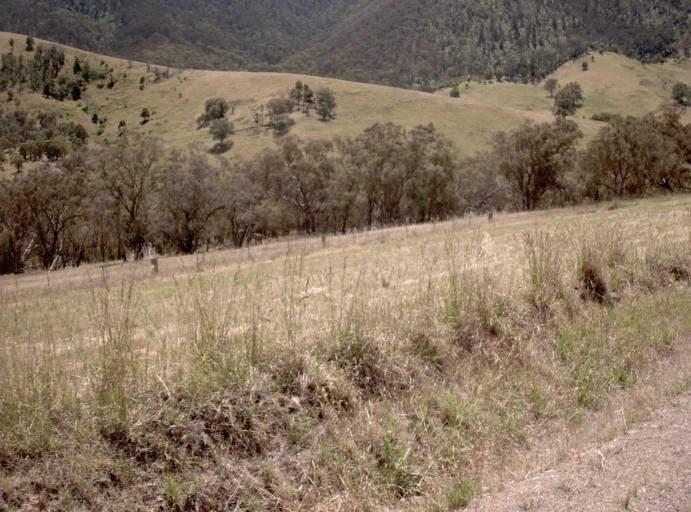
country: AU
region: Victoria
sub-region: East Gippsland
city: Bairnsdale
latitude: -37.1661
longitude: 147.6846
